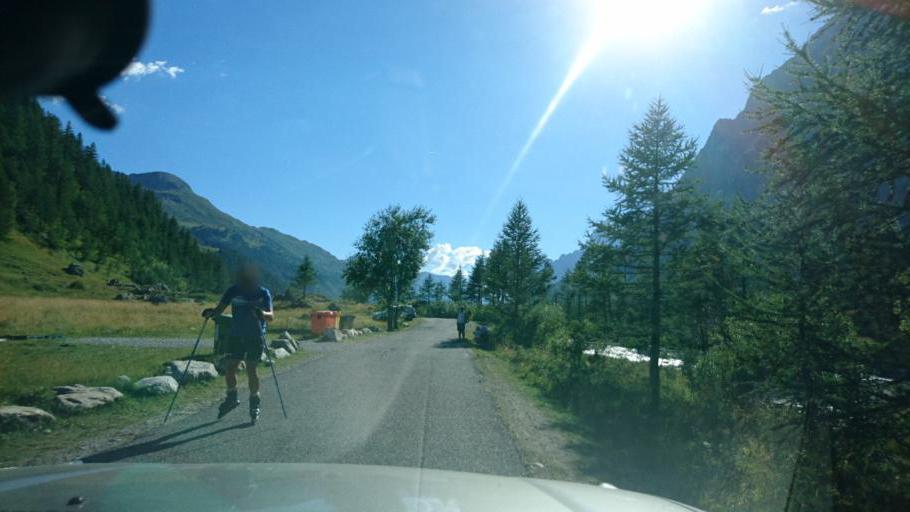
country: IT
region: Aosta Valley
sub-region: Valle d'Aosta
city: Courmayeur
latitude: 45.8590
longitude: 7.0349
